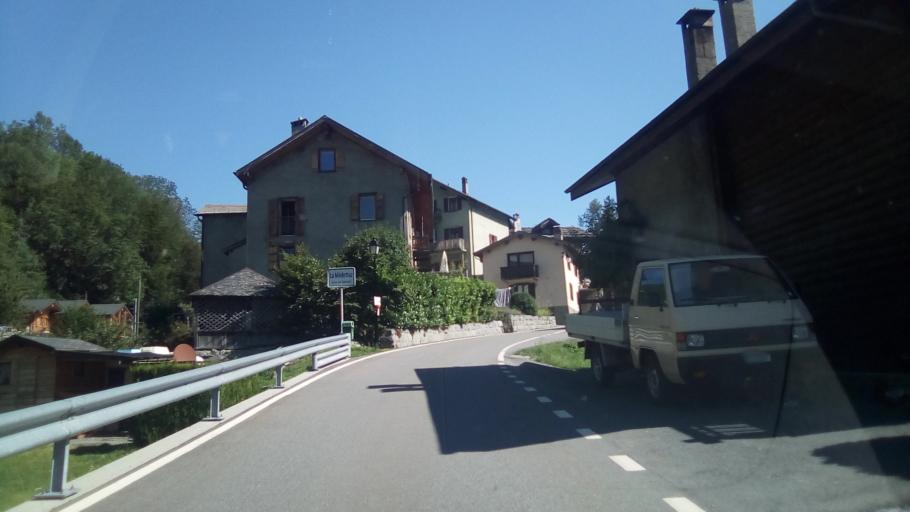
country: CH
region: Valais
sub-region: Saint-Maurice District
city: Salvan
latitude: 46.1081
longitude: 7.0075
